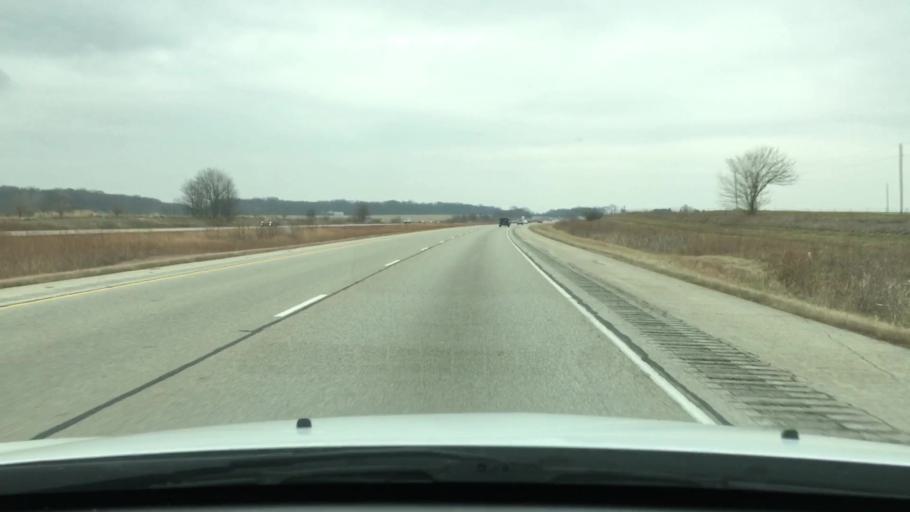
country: US
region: Illinois
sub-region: Logan County
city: Atlanta
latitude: 40.3456
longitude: -89.1306
